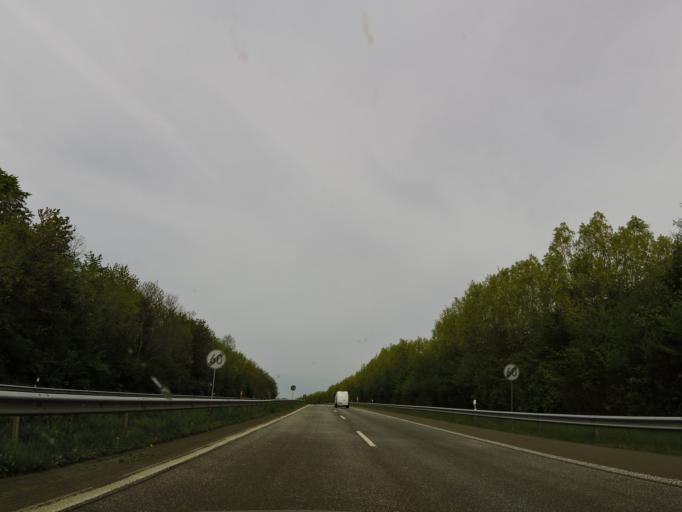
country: DE
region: Schleswig-Holstein
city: Arkebek
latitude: 54.1513
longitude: 9.2377
